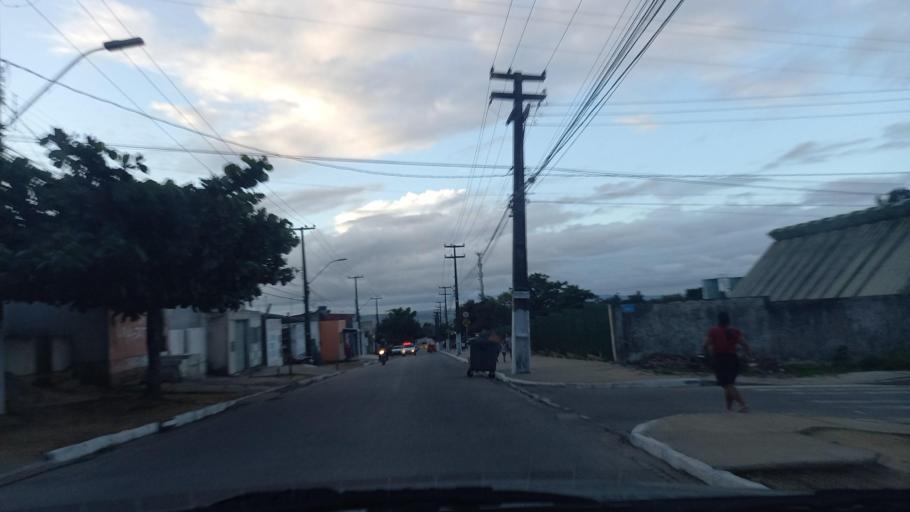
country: BR
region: Pernambuco
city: Garanhuns
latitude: -8.8795
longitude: -36.4658
